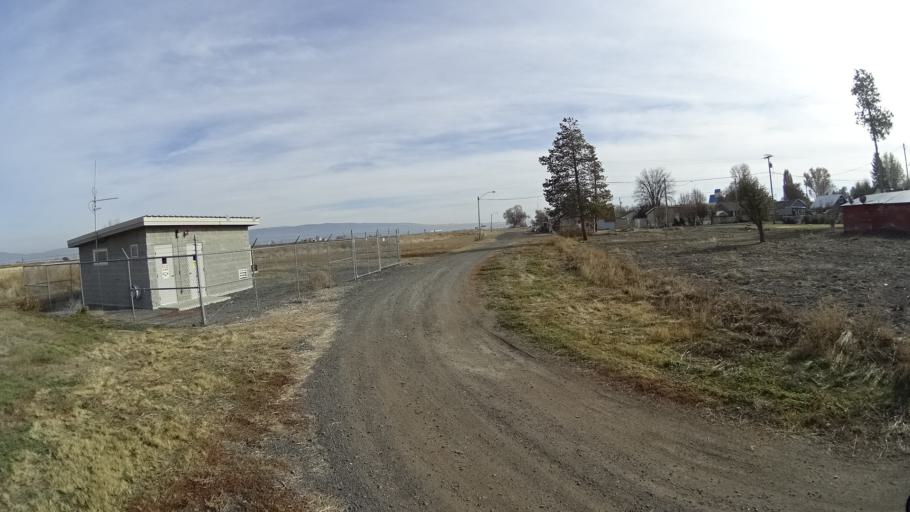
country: US
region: California
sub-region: Siskiyou County
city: Tulelake
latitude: 41.9606
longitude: -121.4812
